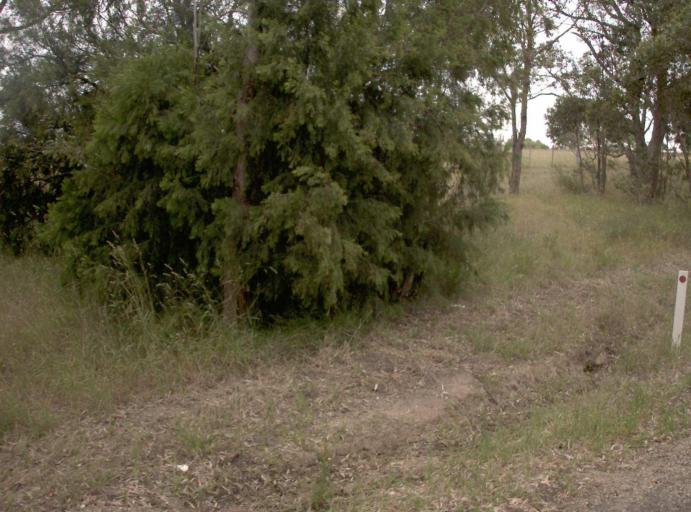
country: AU
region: Victoria
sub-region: East Gippsland
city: Bairnsdale
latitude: -37.7929
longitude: 147.6078
